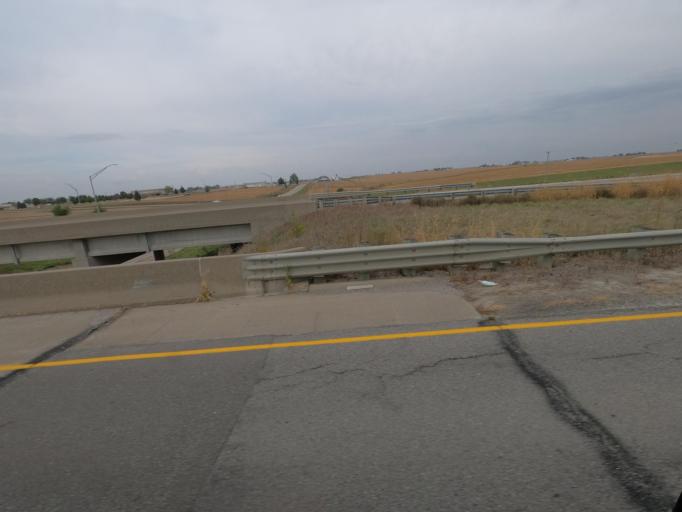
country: US
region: Iowa
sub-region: Marion County
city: Pella
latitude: 41.3894
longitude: -92.8703
